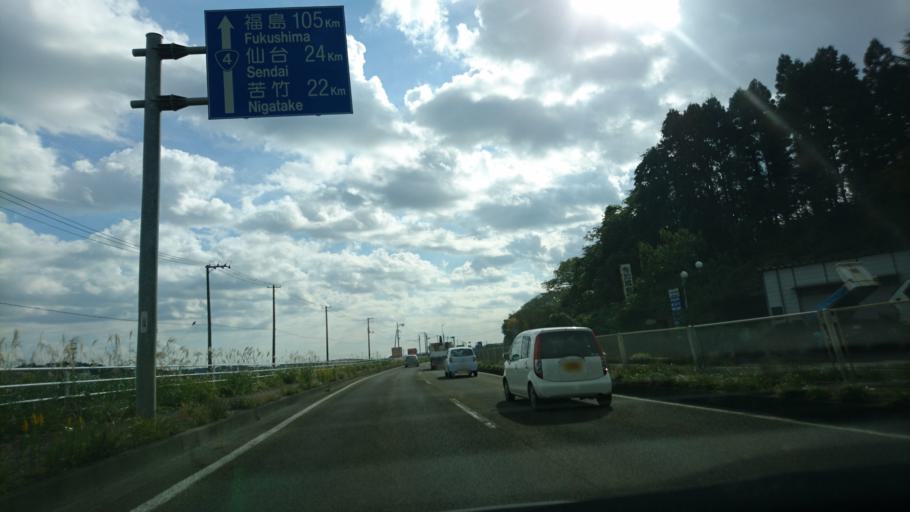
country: JP
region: Miyagi
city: Tomiya
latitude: 38.4520
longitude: 140.8834
